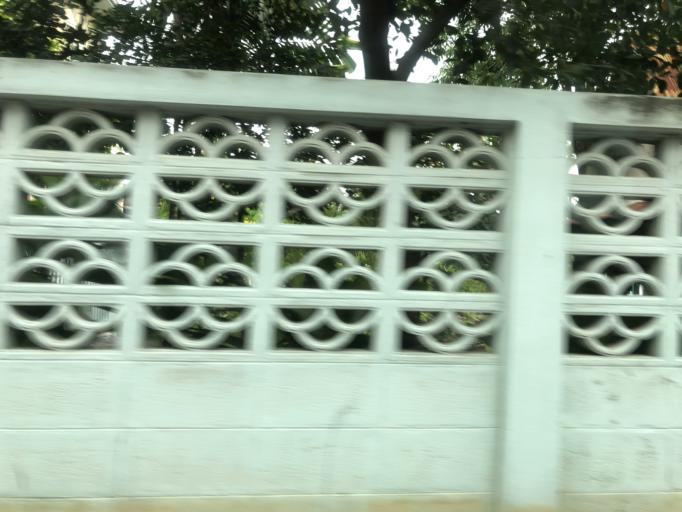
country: TH
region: Bangkok
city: Don Mueang
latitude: 13.9223
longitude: 100.5931
